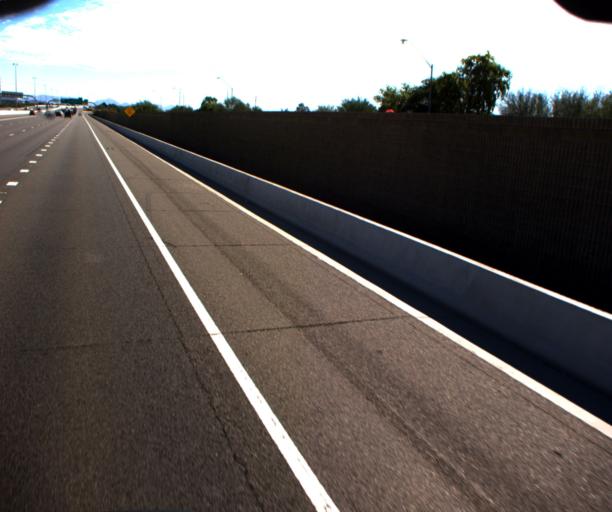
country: US
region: Arizona
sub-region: Maricopa County
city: Peoria
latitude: 33.6694
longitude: -112.1446
